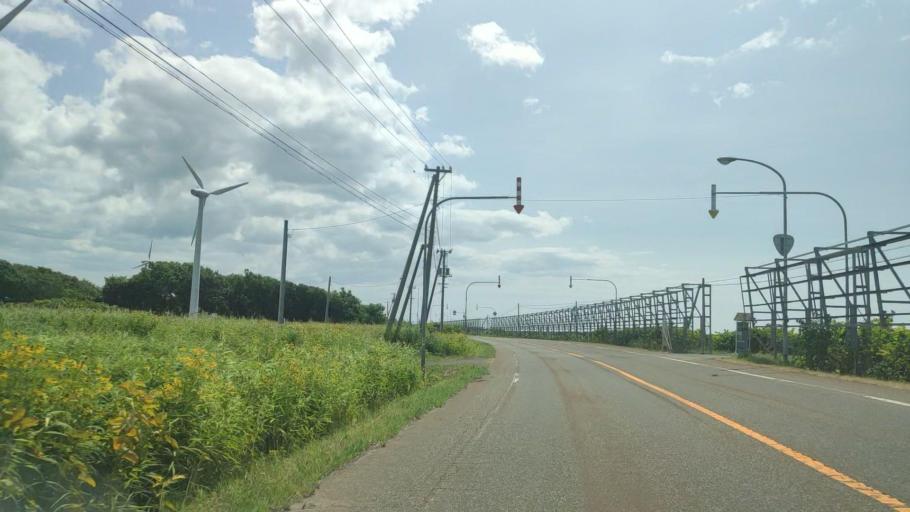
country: JP
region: Hokkaido
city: Makubetsu
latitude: 44.7101
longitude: 141.7897
